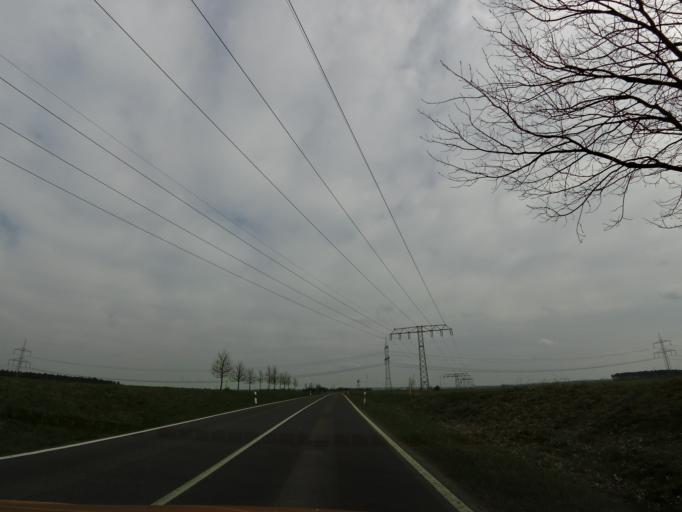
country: DE
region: Brandenburg
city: Briesen
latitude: 52.3518
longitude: 14.3066
